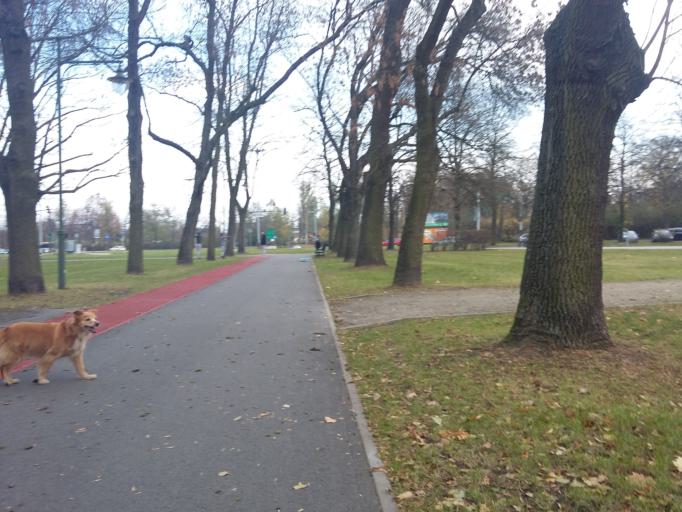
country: PL
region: Lodz Voivodeship
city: Lodz
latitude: 51.7663
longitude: 19.4208
